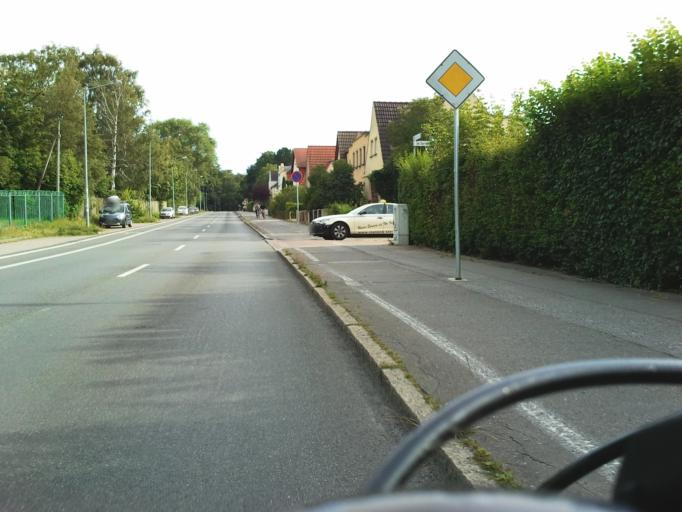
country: DE
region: Mecklenburg-Vorpommern
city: Kritzmow
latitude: 54.0849
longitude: 12.0878
